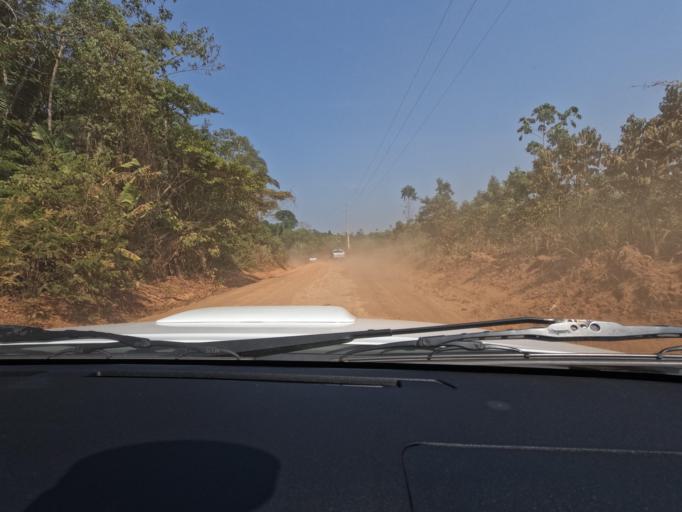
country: BR
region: Rondonia
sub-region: Porto Velho
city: Porto Velho
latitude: -8.6703
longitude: -64.0022
